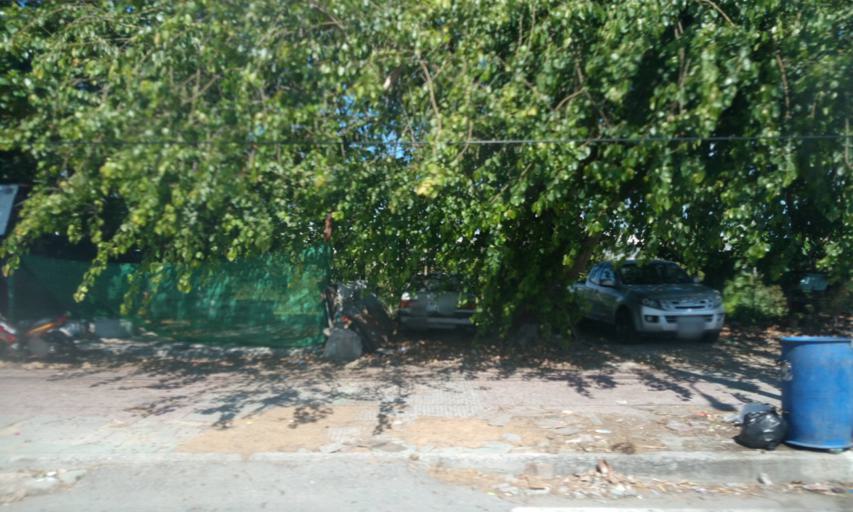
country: TH
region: Samut Prakan
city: Bang Bo District
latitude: 13.5583
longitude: 100.7891
